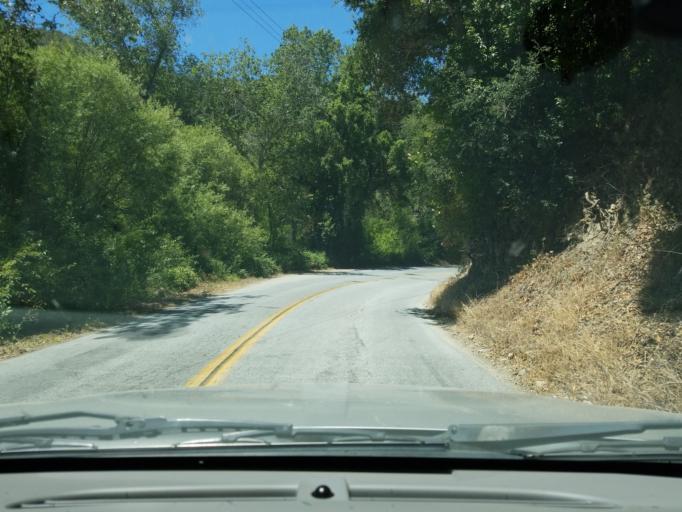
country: US
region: California
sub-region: Monterey County
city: Carmel Valley Village
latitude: 36.4482
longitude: -121.6871
